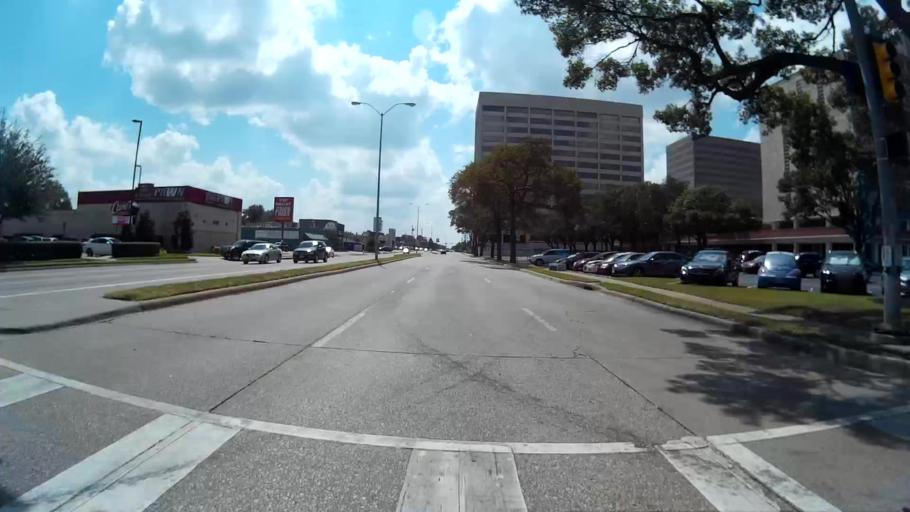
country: US
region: Texas
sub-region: Dallas County
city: Highland Park
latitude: 32.8489
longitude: -96.7701
